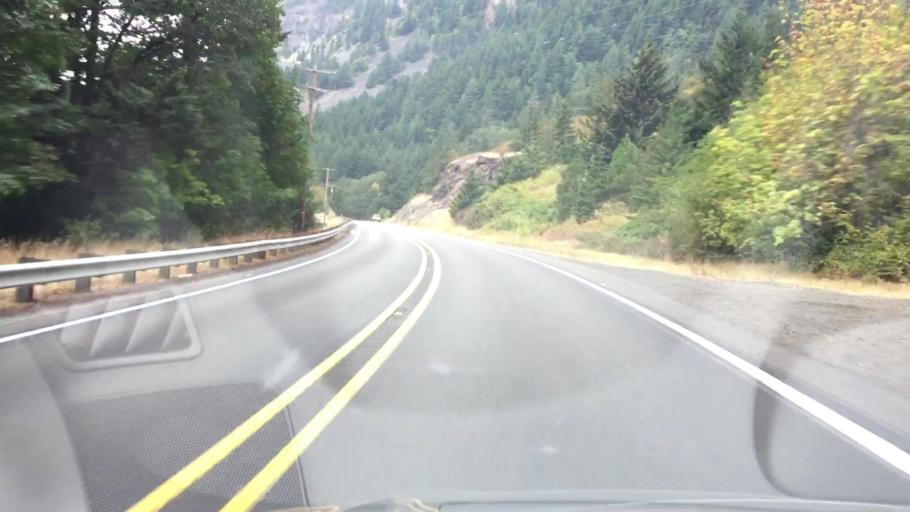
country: US
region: Washington
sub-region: Skamania County
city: Carson
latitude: 45.7010
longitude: -121.7409
